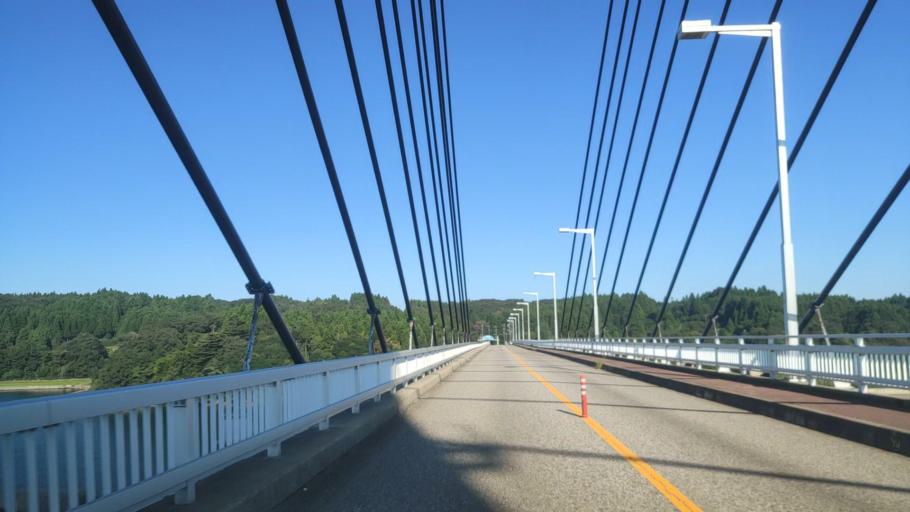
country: JP
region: Ishikawa
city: Nanao
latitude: 37.1358
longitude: 136.9036
